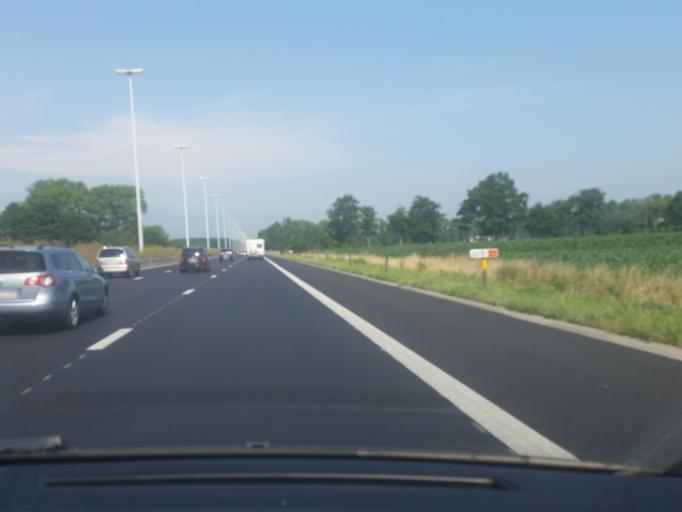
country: BE
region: Flanders
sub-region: Provincie Oost-Vlaanderen
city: Aalter
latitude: 51.0901
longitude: 3.4124
